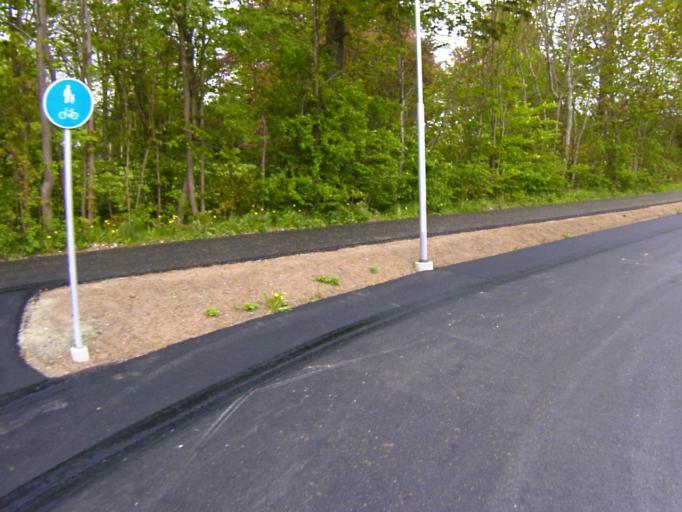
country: SE
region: Skane
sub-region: Kristianstads Kommun
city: Kristianstad
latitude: 56.0177
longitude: 14.1982
